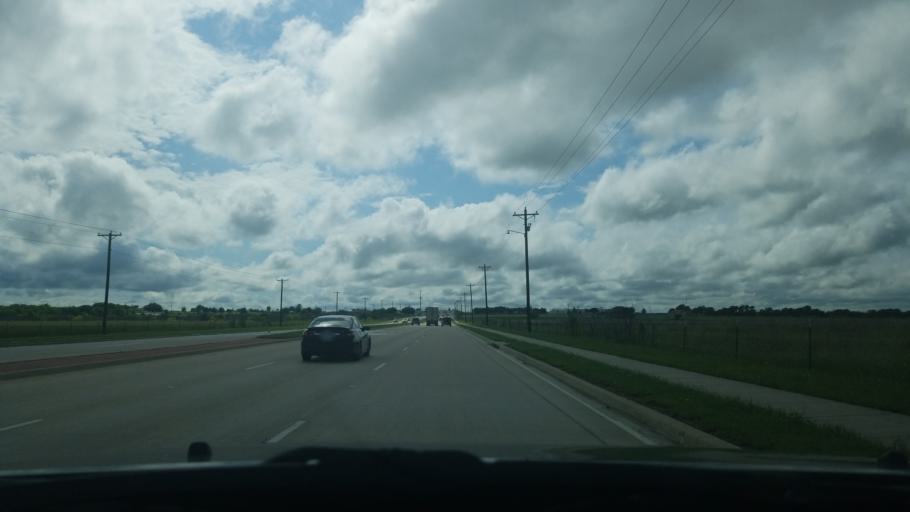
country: US
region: Texas
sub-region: Denton County
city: Krum
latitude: 33.2332
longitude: -97.2347
